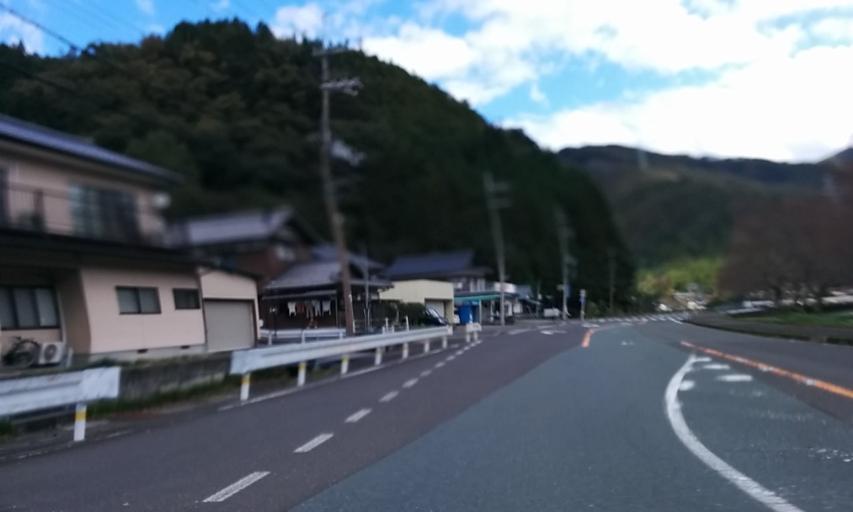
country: JP
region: Fukui
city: Obama
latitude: 35.4006
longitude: 135.6866
